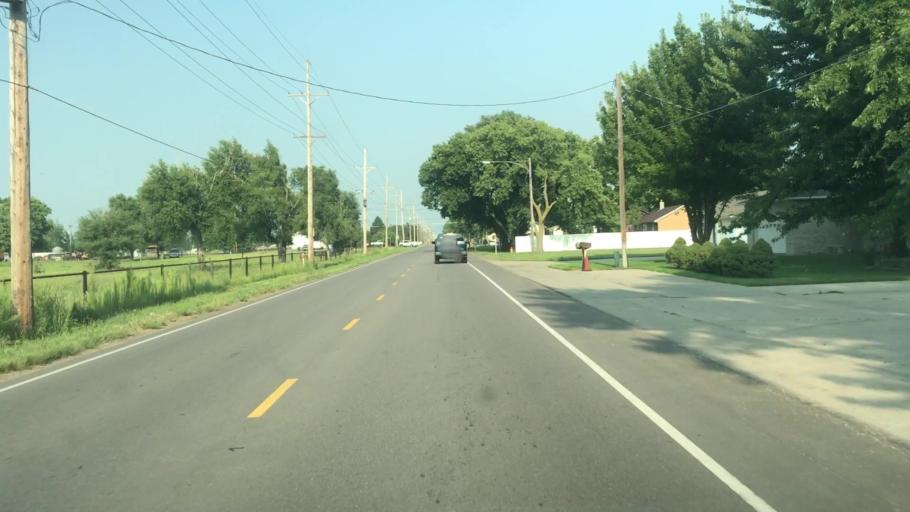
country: US
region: Nebraska
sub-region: Hall County
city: Grand Island
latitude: 40.9457
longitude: -98.3422
